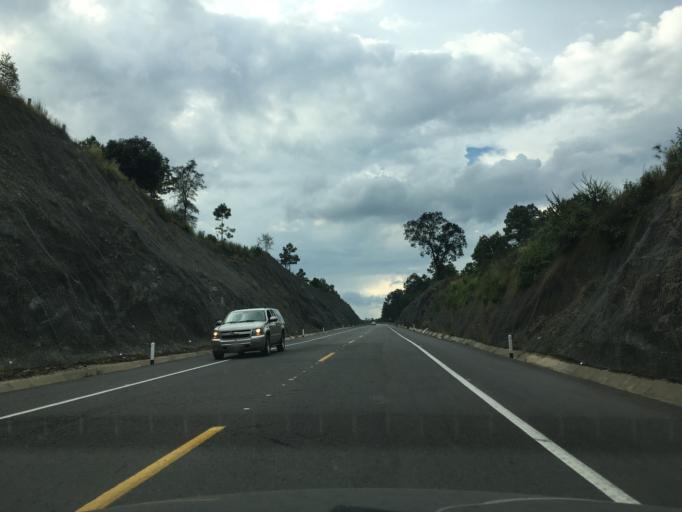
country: MX
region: Michoacan
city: Angahuan
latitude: 19.5142
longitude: -102.1697
